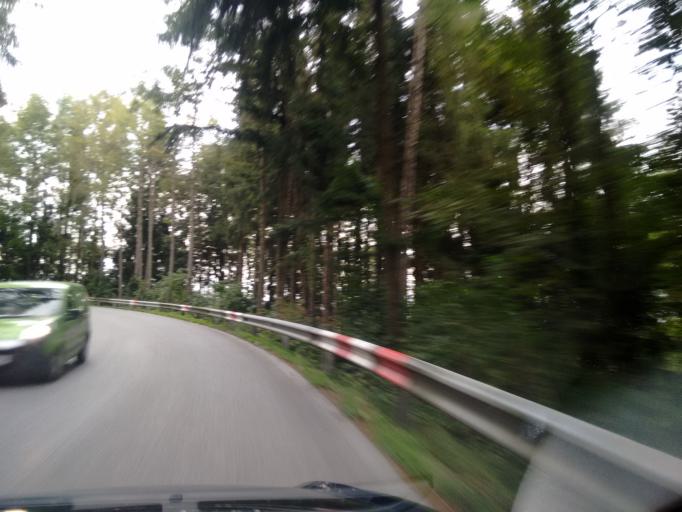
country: AT
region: Upper Austria
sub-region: Politischer Bezirk Steyr-Land
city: Bad Hall
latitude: 48.0418
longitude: 14.1972
